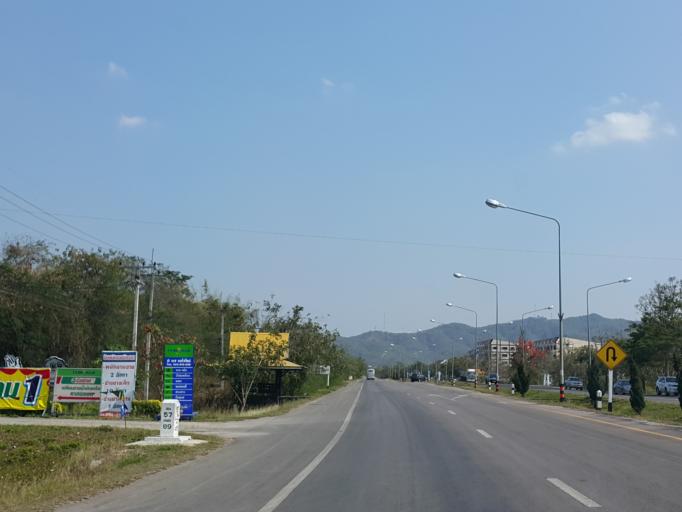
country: TH
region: Lampang
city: Lampang
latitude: 18.2730
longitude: 99.5235
